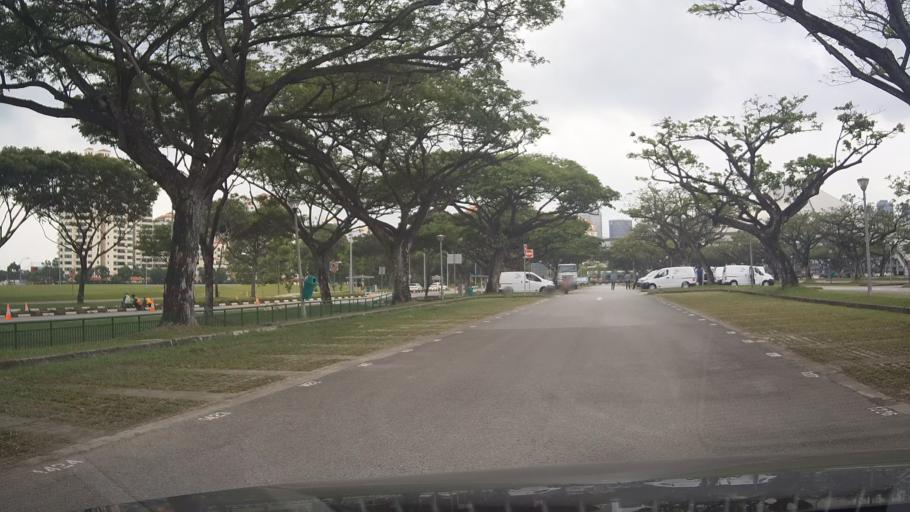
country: SG
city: Singapore
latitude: 1.3014
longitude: 103.8779
